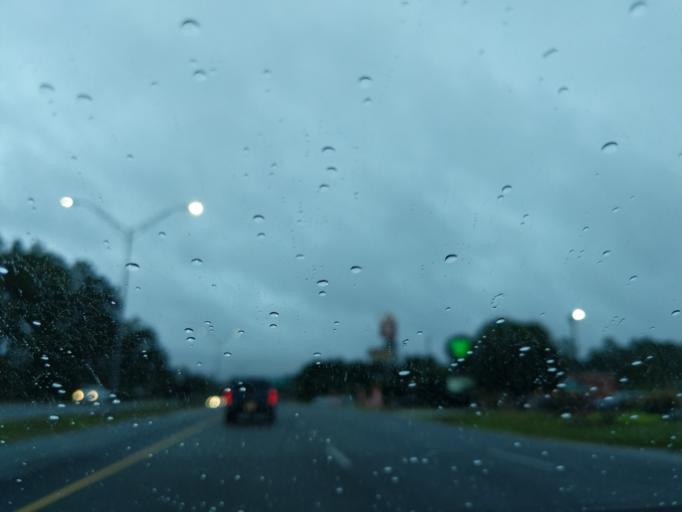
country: US
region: Texas
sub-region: Angelina County
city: Lufkin
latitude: 31.2881
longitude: -94.7298
